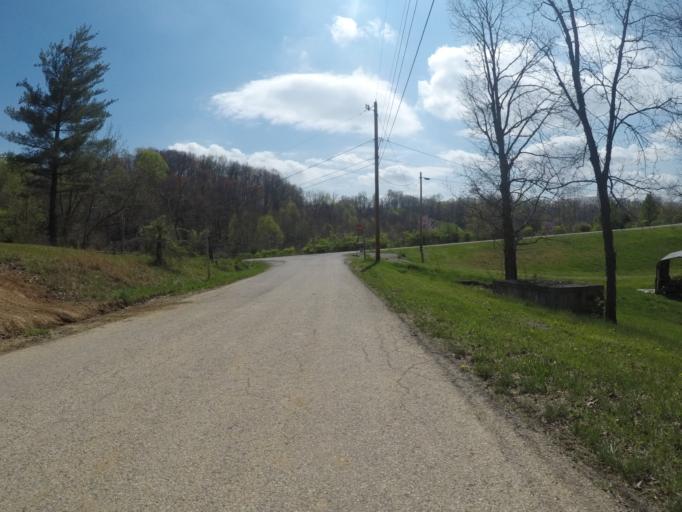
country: US
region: Ohio
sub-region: Lawrence County
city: Burlington
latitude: 38.3861
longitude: -82.5323
